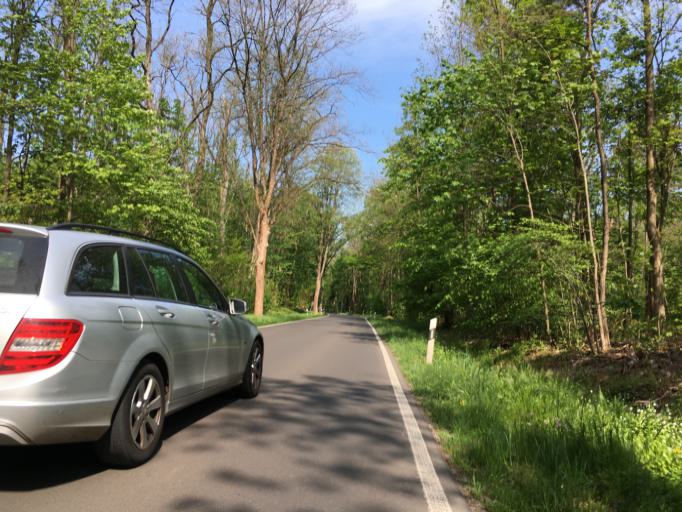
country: DE
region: Brandenburg
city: Werneuchen
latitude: 52.6152
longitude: 13.7538
